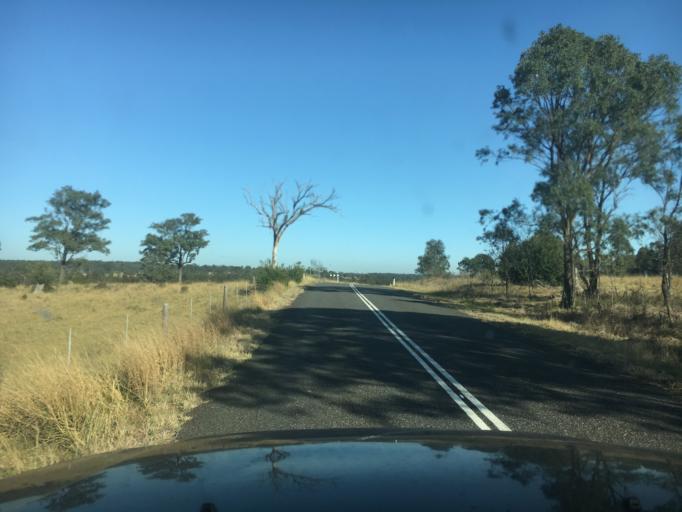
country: AU
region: New South Wales
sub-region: Singleton
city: Singleton
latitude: -32.5503
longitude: 151.2697
